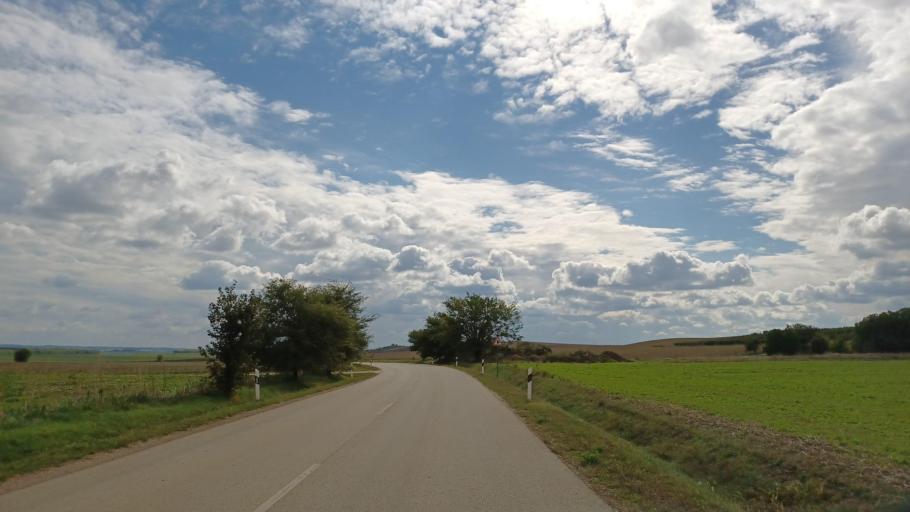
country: HU
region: Tolna
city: Simontornya
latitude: 46.7097
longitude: 18.5811
